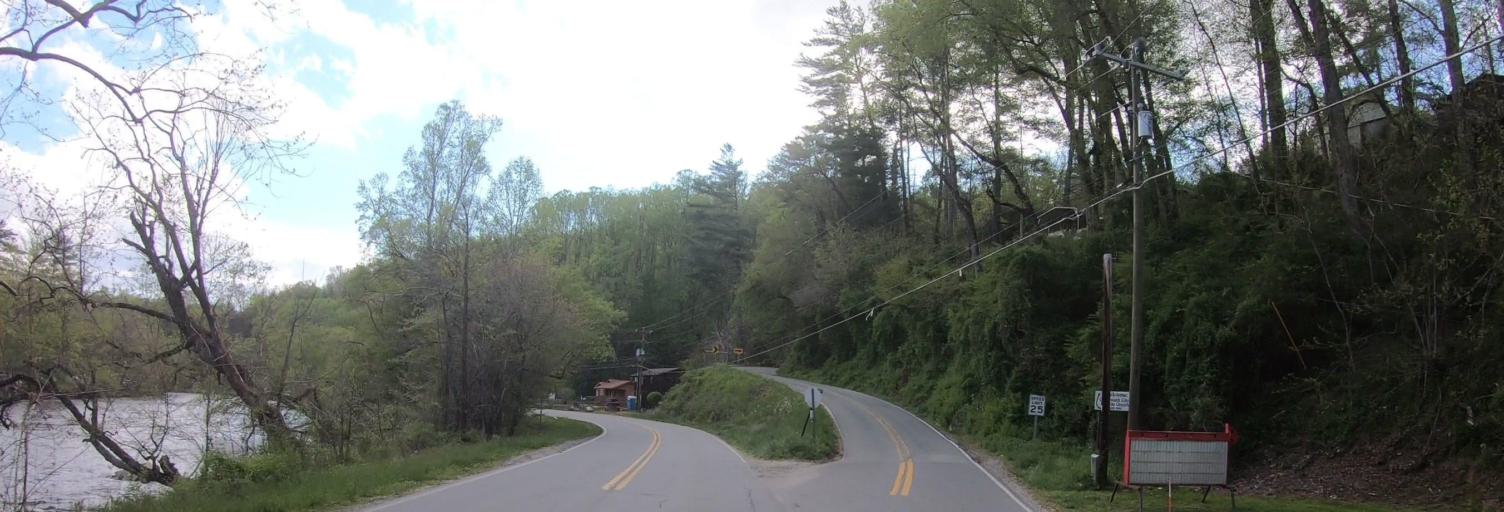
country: US
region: North Carolina
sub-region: Swain County
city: Bryson City
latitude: 35.4528
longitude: -83.3982
